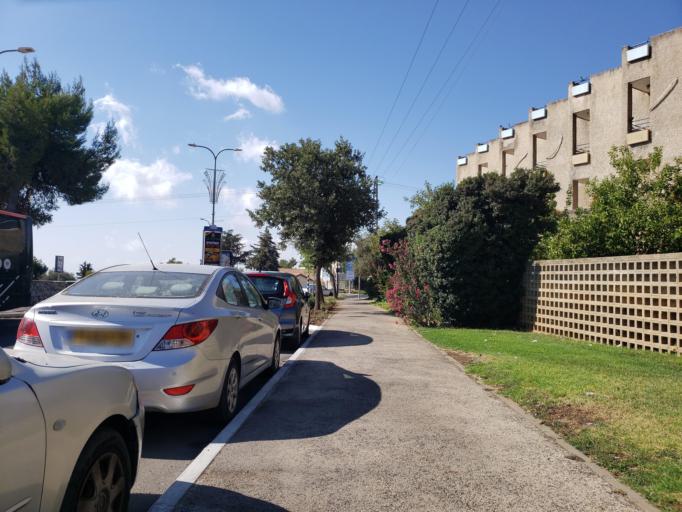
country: IL
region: Northern District
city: Safed
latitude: 32.9637
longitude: 35.4982
